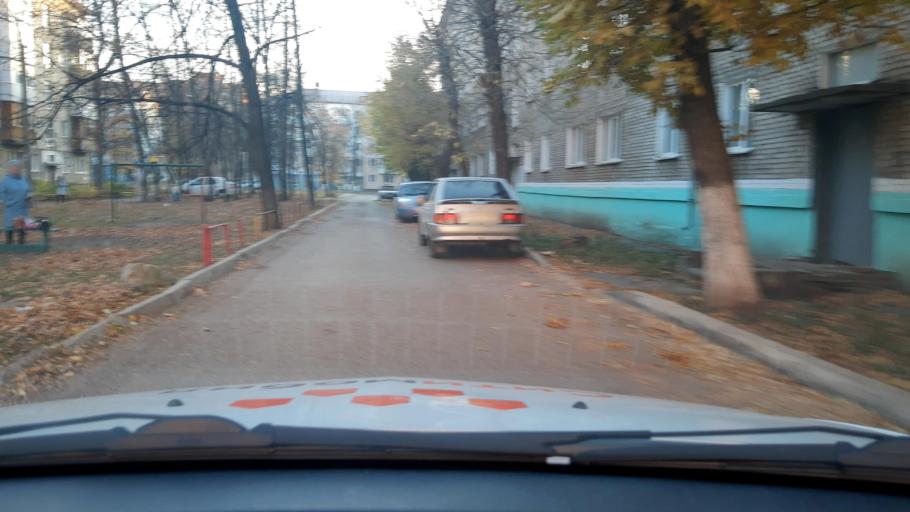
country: RU
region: Bashkortostan
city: Ufa
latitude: 54.7525
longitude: 55.9912
